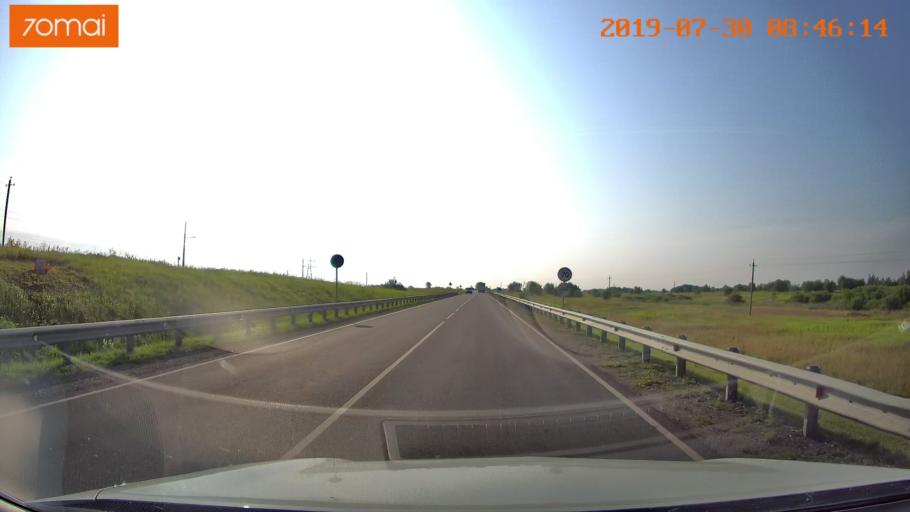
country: RU
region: Kaliningrad
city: Chernyakhovsk
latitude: 54.6245
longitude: 21.8803
